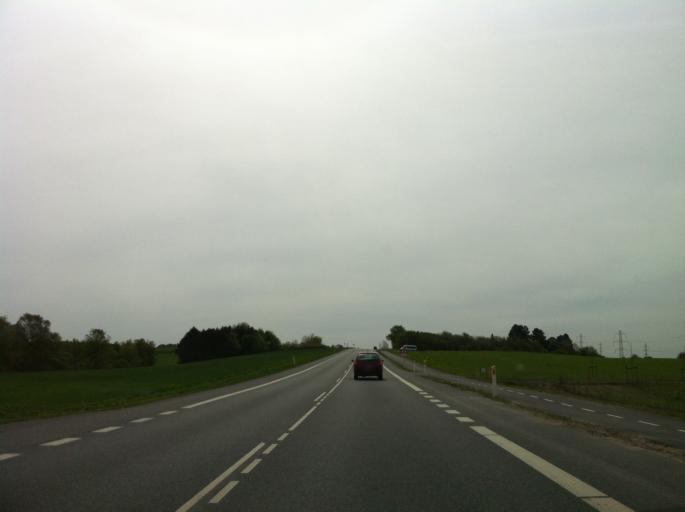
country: DK
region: Capital Region
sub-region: Frederikssund Kommune
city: Slangerup
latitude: 55.8270
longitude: 12.1633
